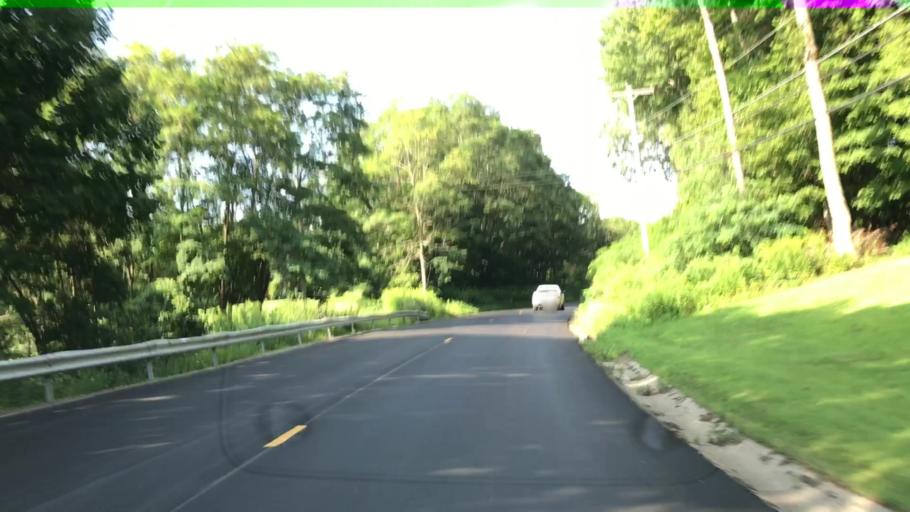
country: US
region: New York
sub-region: Chautauqua County
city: Fredonia
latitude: 42.3317
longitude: -79.3258
